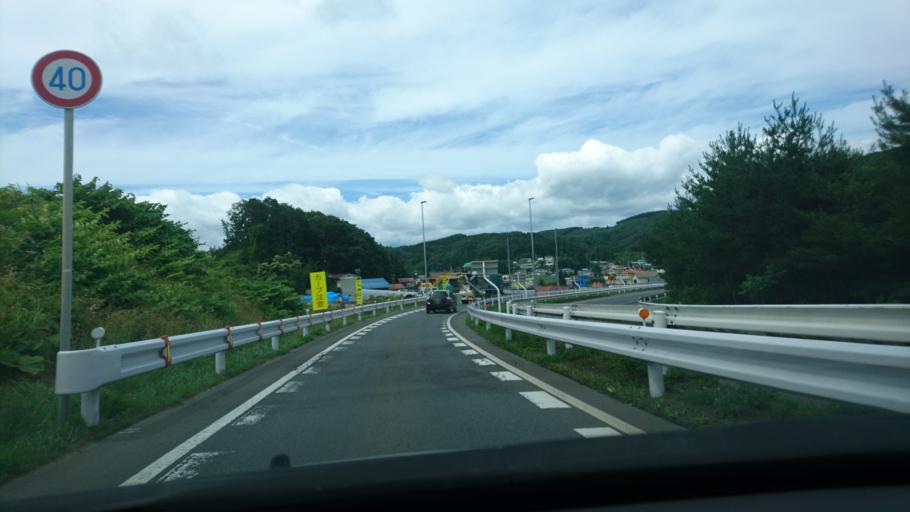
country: JP
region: Aomori
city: Hachinohe
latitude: 40.2207
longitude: 141.7824
